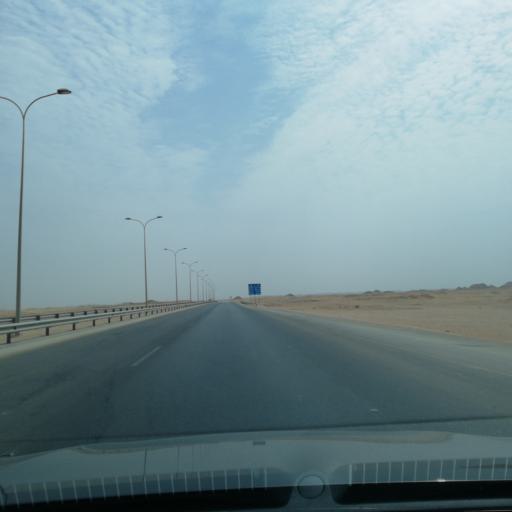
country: OM
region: Zufar
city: Salalah
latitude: 17.6408
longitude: 54.0441
